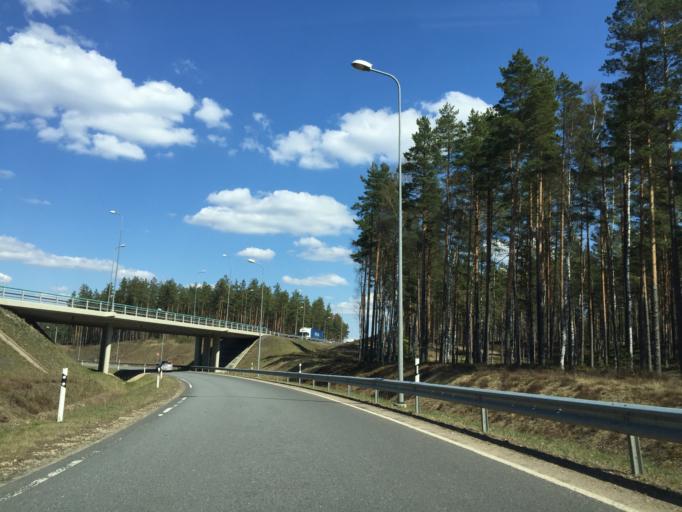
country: LV
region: Saulkrastu
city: Saulkrasti
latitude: 57.1942
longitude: 24.3625
